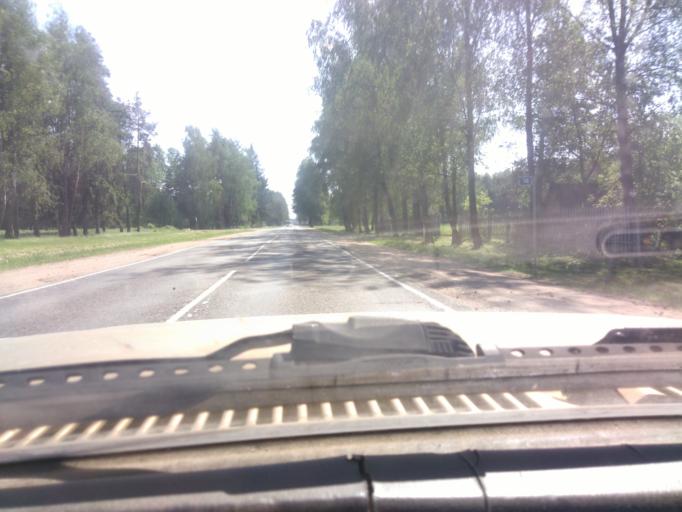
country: BY
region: Mogilev
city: Palykavichy Pyershyya
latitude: 53.9897
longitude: 30.3184
